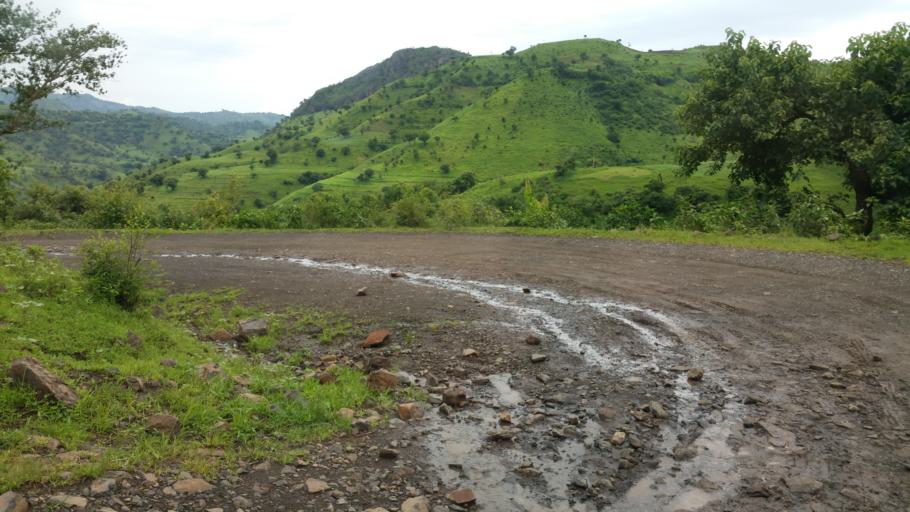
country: ET
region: Amhara
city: Debark'
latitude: 13.2802
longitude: 37.8713
